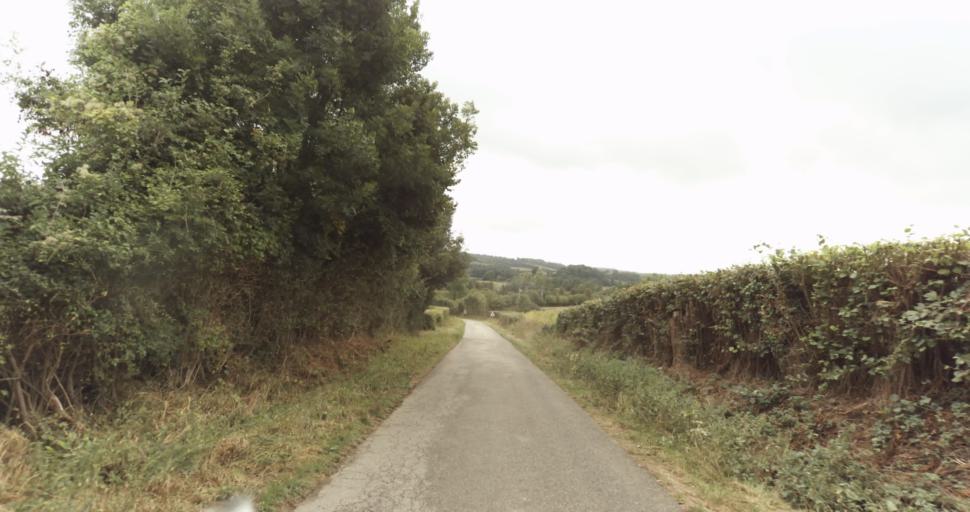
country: FR
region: Lower Normandy
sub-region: Departement de l'Orne
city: Gace
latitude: 48.8728
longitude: 0.2730
